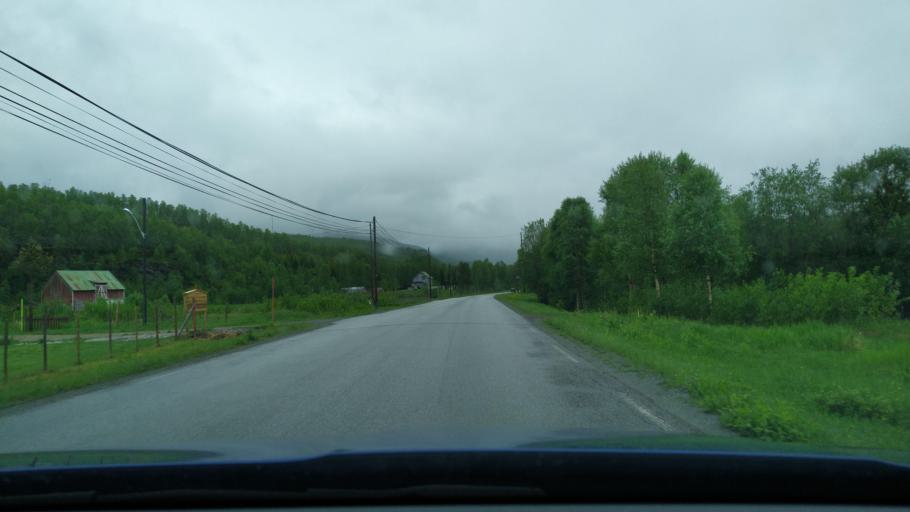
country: NO
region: Troms
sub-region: Dyroy
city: Brostadbotn
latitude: 69.0706
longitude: 17.7341
